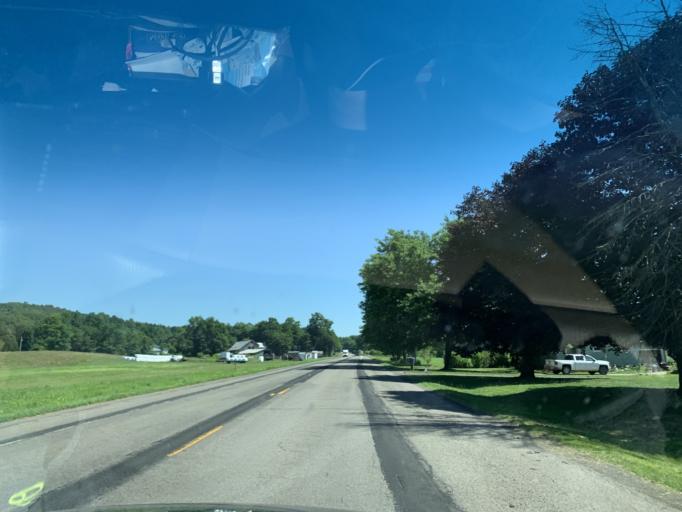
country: US
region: New York
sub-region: Delaware County
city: Sidney
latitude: 42.3907
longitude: -75.4027
